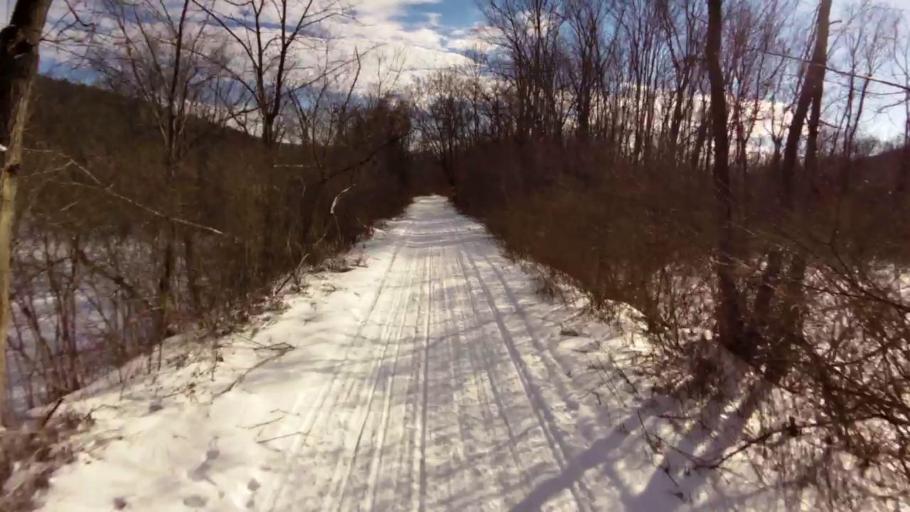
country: US
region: Pennsylvania
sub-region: McKean County
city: Foster Brook
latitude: 42.0022
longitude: -78.6221
